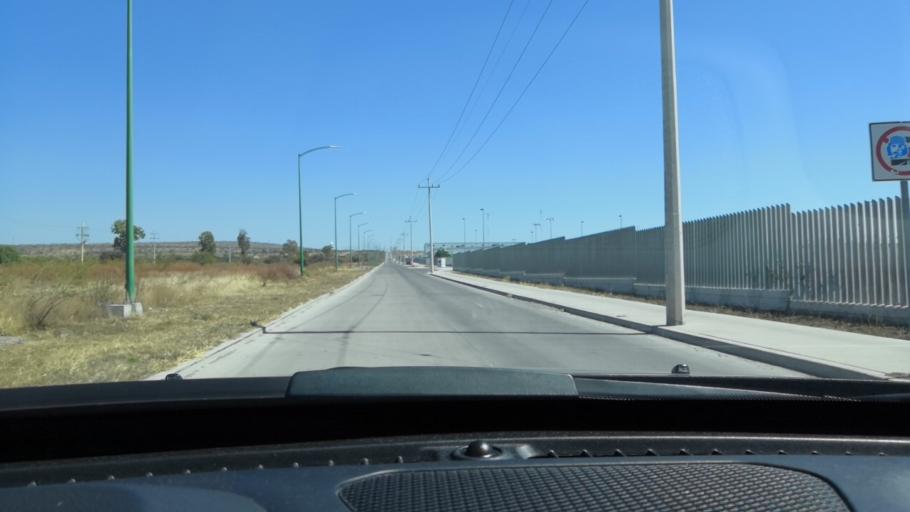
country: MX
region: Guanajuato
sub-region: Leon
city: Centro Familiar la Soledad
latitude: 21.1025
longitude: -101.7716
